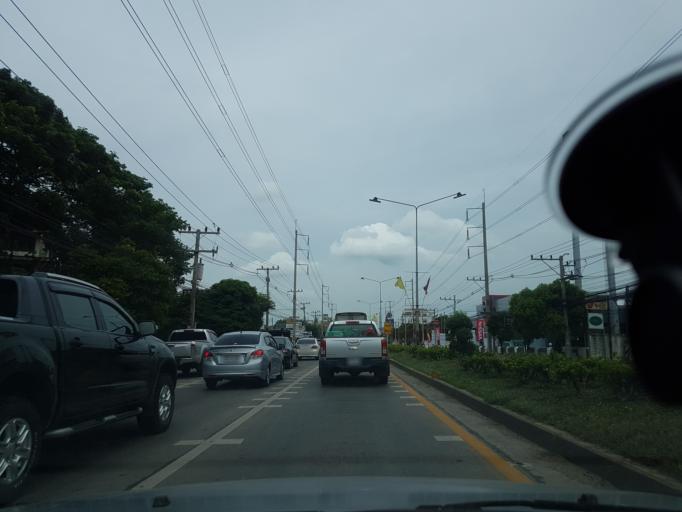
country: TH
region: Lop Buri
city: Lop Buri
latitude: 14.7958
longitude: 100.6661
